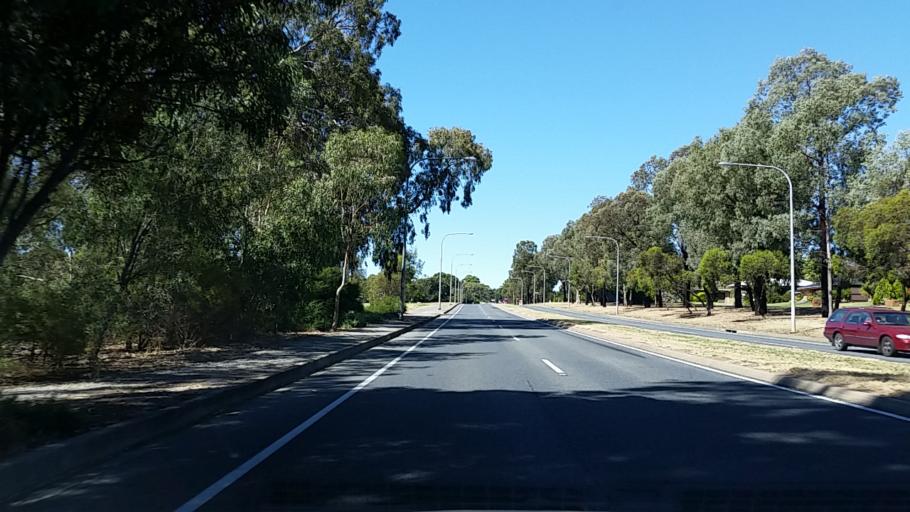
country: AU
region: South Australia
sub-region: Tea Tree Gully
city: Hope Valley
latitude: -34.8110
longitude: 138.6960
